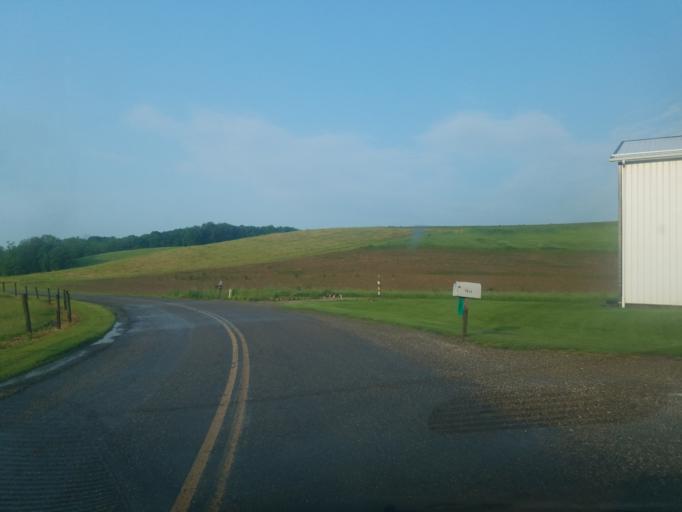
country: US
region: Ohio
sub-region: Stark County
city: Minerva
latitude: 40.6776
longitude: -81.1097
